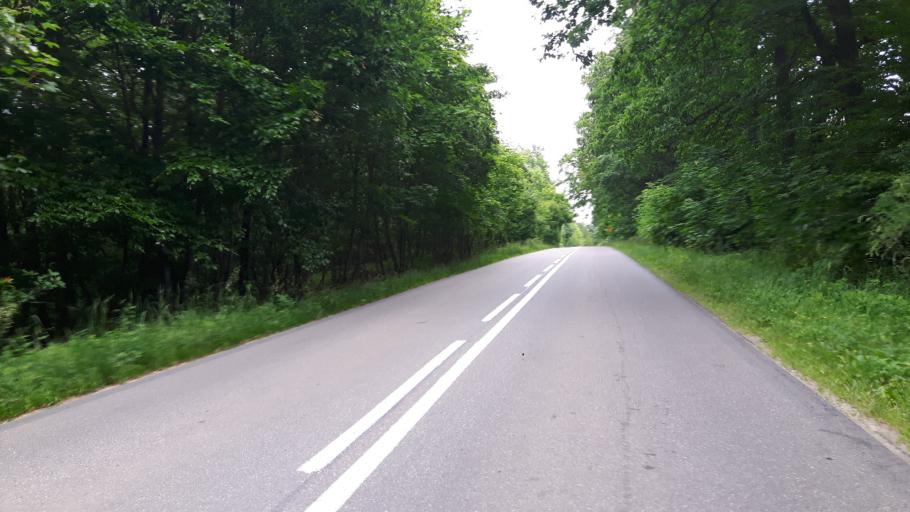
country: PL
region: Pomeranian Voivodeship
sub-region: Powiat leborski
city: Leba
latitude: 54.7532
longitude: 17.6815
